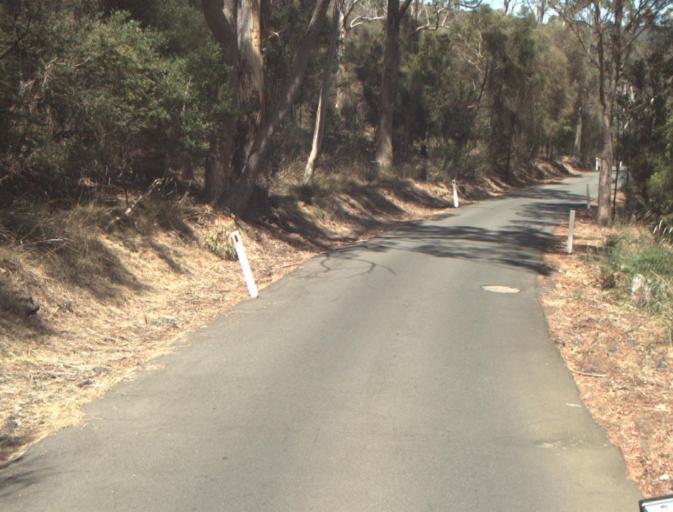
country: AU
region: Tasmania
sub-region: Launceston
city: Summerhill
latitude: -41.4575
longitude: 147.1190
